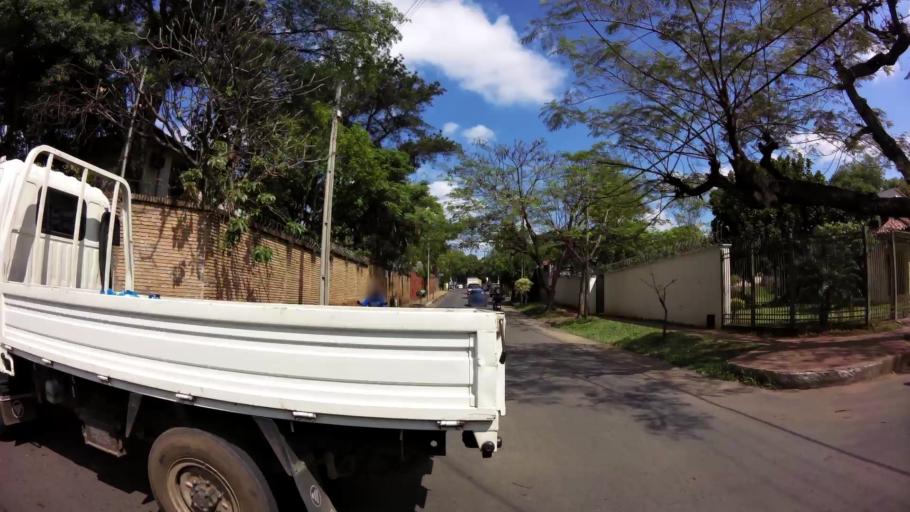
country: PY
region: Central
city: San Lorenzo
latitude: -25.3391
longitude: -57.5069
